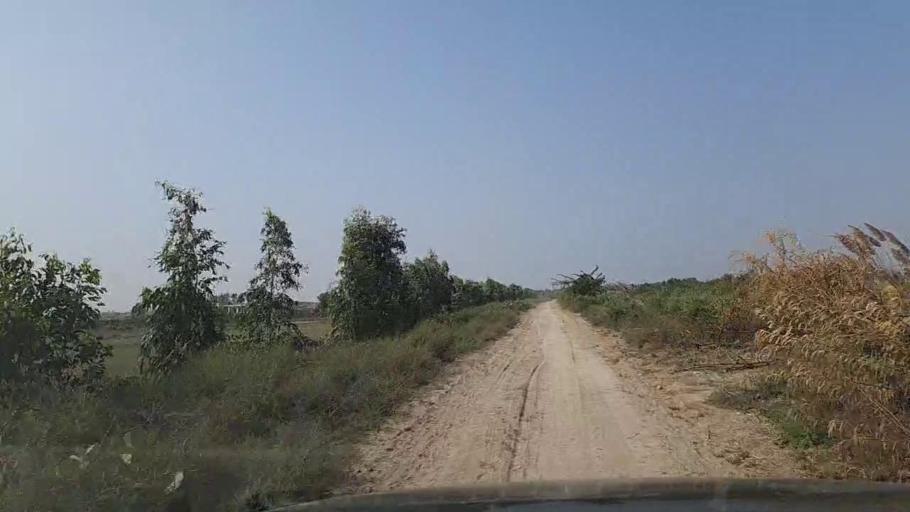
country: PK
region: Sindh
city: Gharo
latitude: 24.7292
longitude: 67.7212
